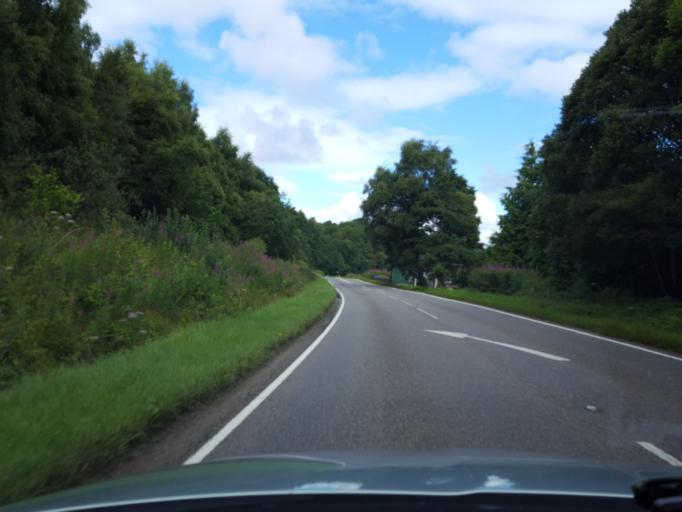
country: GB
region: Scotland
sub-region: Moray
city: Rothes
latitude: 57.5077
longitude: -3.2000
